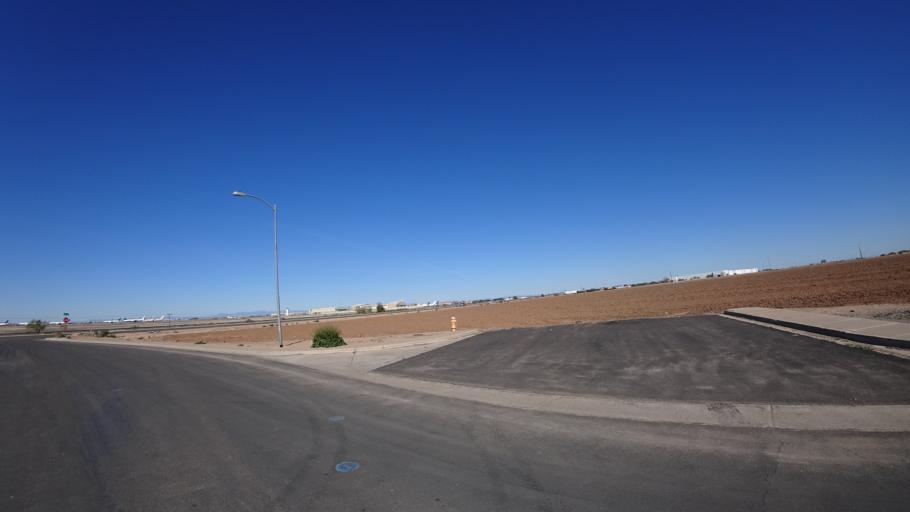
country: US
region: Arizona
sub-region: Maricopa County
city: Goodyear
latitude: 33.4165
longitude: -112.3703
